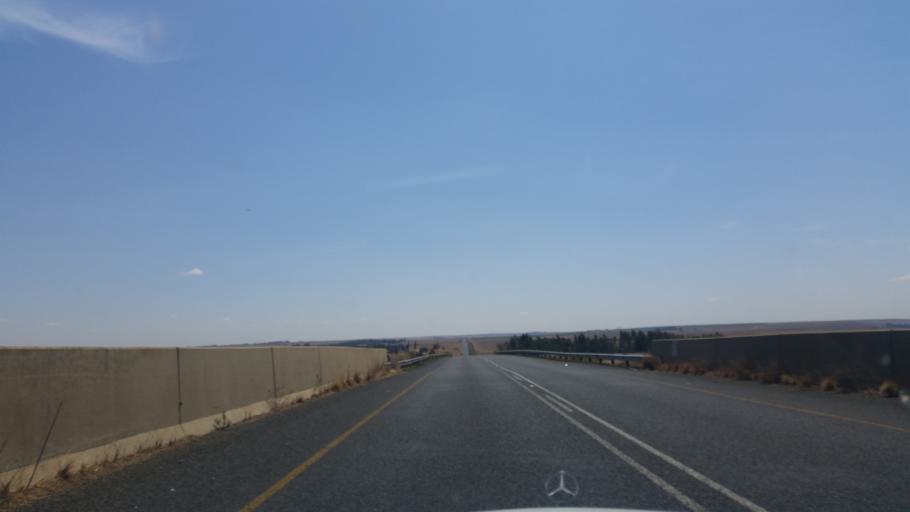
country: ZA
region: Orange Free State
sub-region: Thabo Mofutsanyana District Municipality
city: Phuthaditjhaba
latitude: -28.2035
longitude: 28.6881
